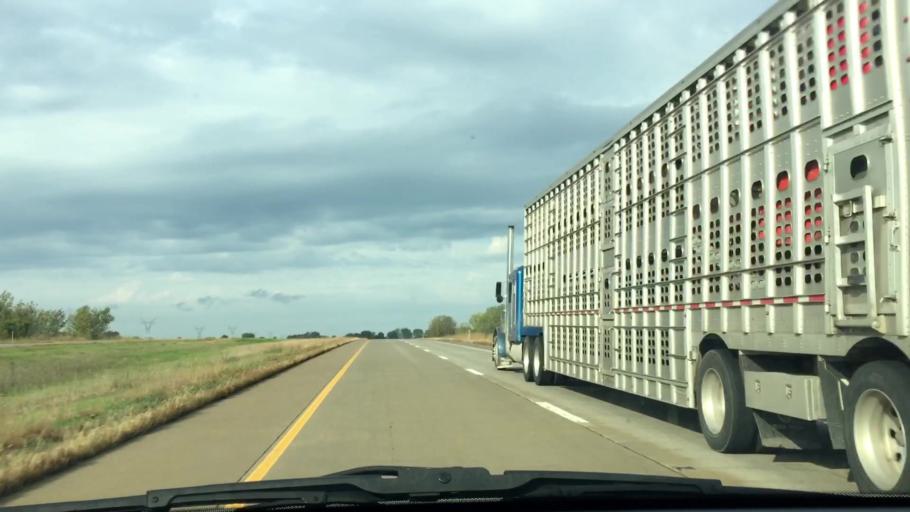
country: US
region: Illinois
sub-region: Whiteside County
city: Sterling
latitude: 41.7657
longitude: -89.8311
